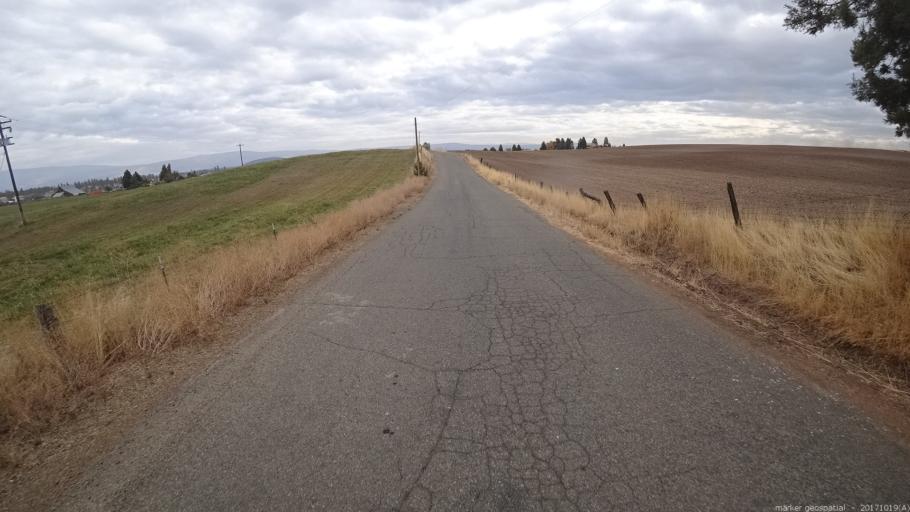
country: US
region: California
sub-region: Shasta County
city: Burney
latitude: 41.0446
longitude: -121.3793
